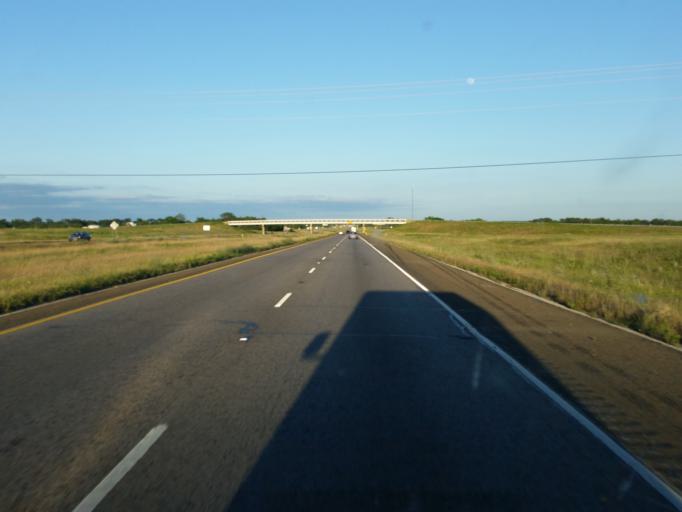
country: US
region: Texas
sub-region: Van Zandt County
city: Wills Point
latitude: 32.6562
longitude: -96.0980
